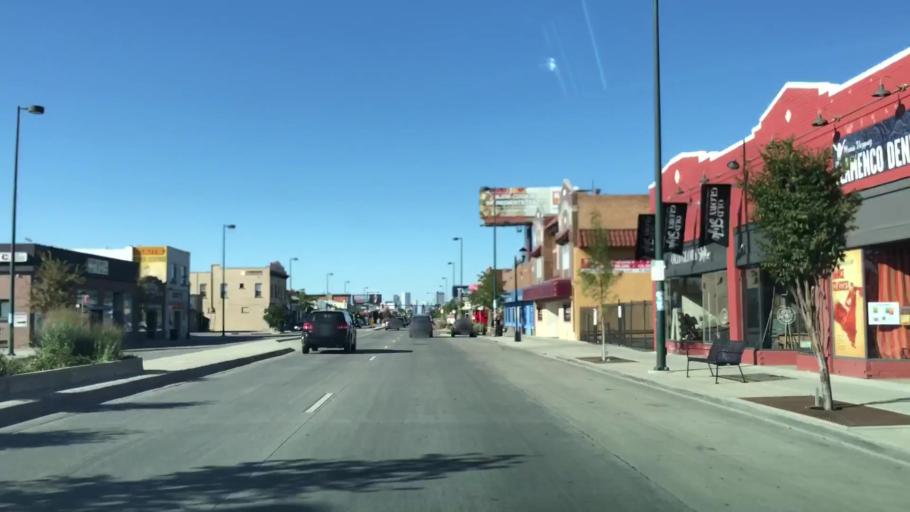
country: US
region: Colorado
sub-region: Arapahoe County
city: Englewood
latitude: 39.6813
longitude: -104.9875
